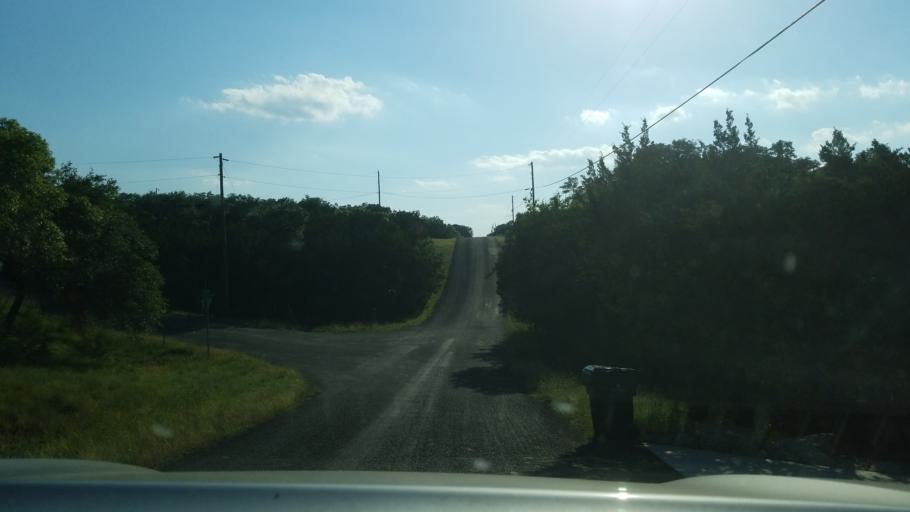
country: US
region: Texas
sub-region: Comal County
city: Bulverde
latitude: 29.7828
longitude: -98.4461
